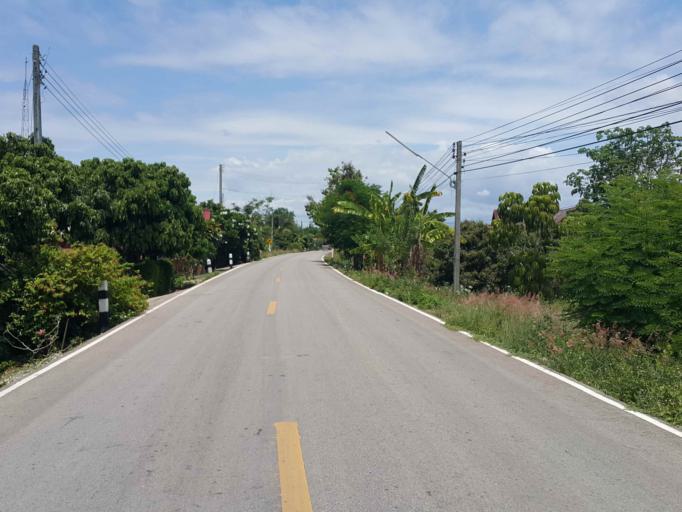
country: TH
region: Lamphun
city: Pa Sang
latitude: 18.5161
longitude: 98.8831
